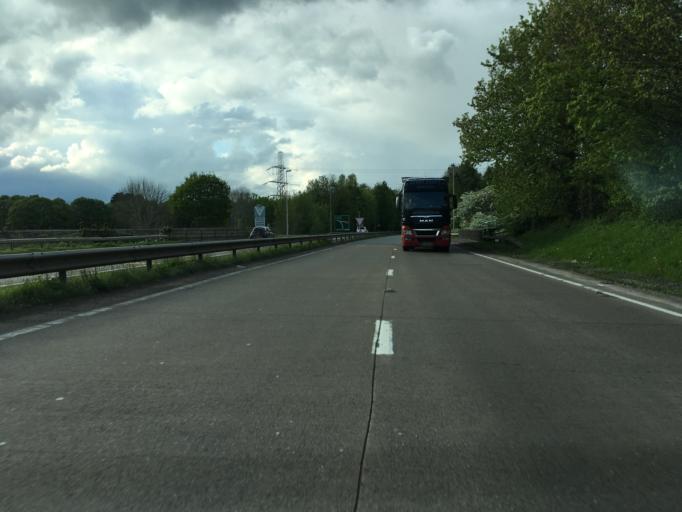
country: GB
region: Wales
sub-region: Monmouthshire
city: Abergavenny
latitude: 51.8050
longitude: -3.0054
